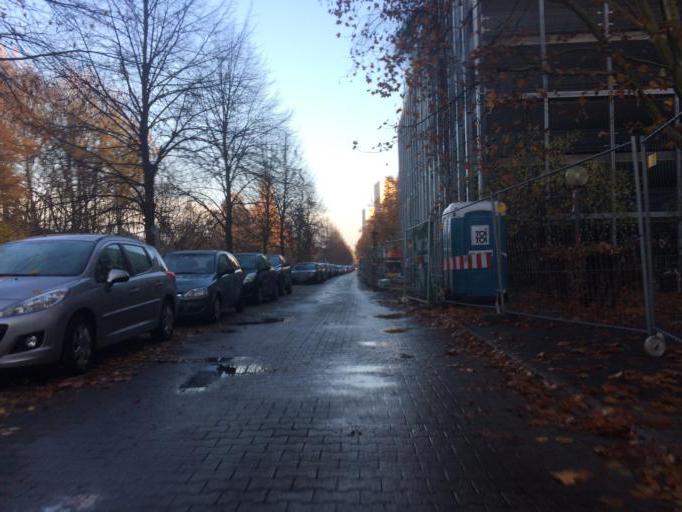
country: DE
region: Berlin
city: Markisches Viertel
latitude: 52.6070
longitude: 13.3582
